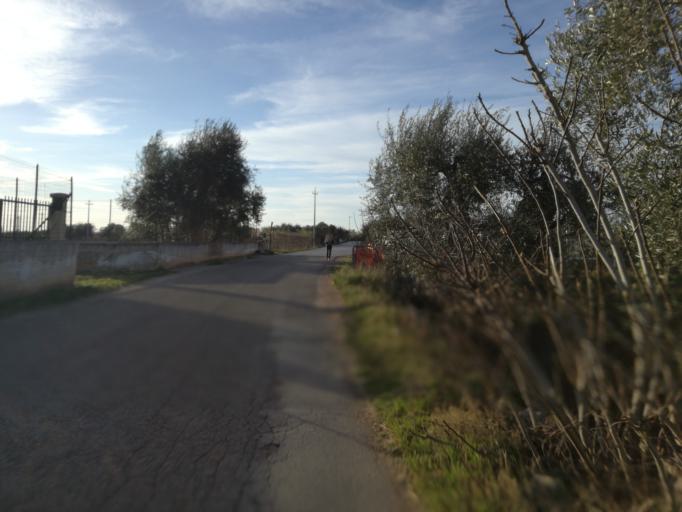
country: IT
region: Apulia
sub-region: Provincia di Bari
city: Valenzano
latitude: 41.0518
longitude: 16.8986
